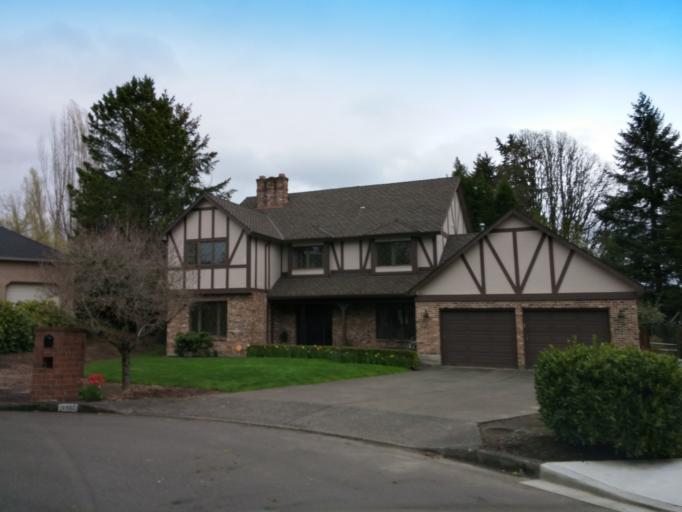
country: US
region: Oregon
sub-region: Washington County
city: Oak Hills
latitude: 45.5222
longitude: -122.8520
